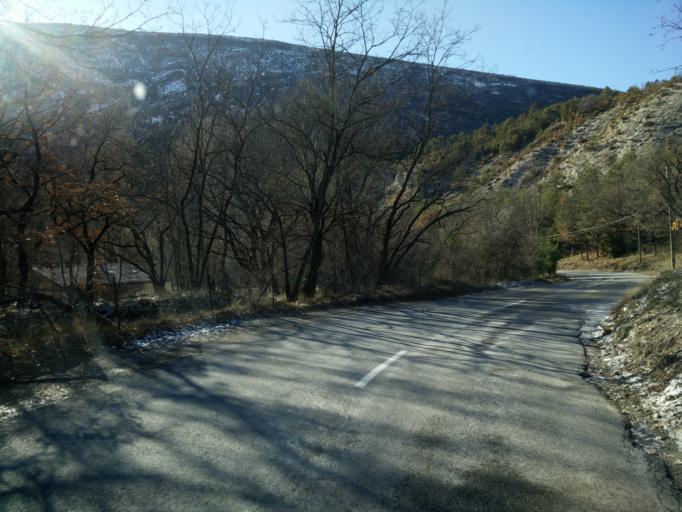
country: FR
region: Provence-Alpes-Cote d'Azur
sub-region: Departement des Alpes-de-Haute-Provence
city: Castellane
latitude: 43.8297
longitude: 6.4274
